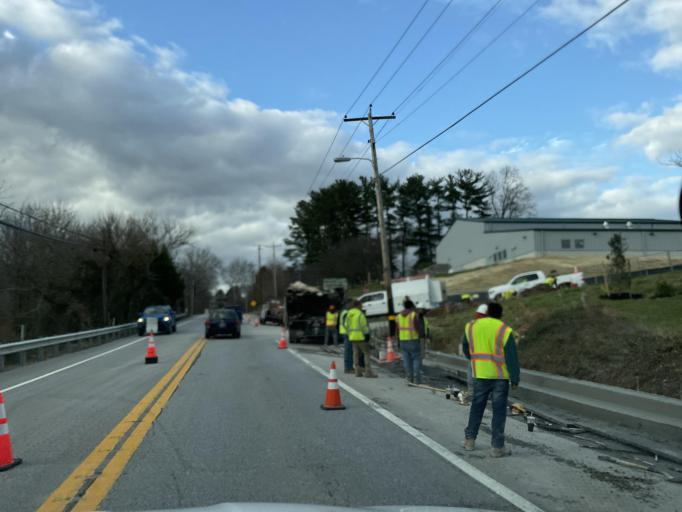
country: US
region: Pennsylvania
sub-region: Adams County
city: Mount Pleasant
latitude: 39.6760
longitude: -77.0355
